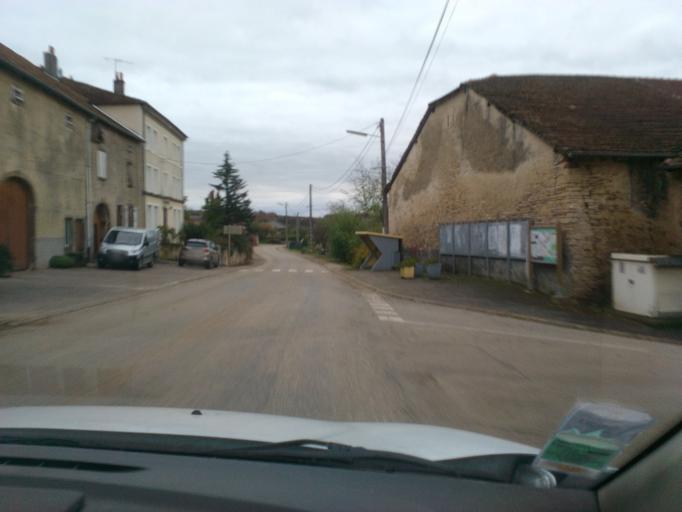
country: FR
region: Lorraine
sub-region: Departement des Vosges
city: Mirecourt
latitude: 48.2848
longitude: 6.1942
